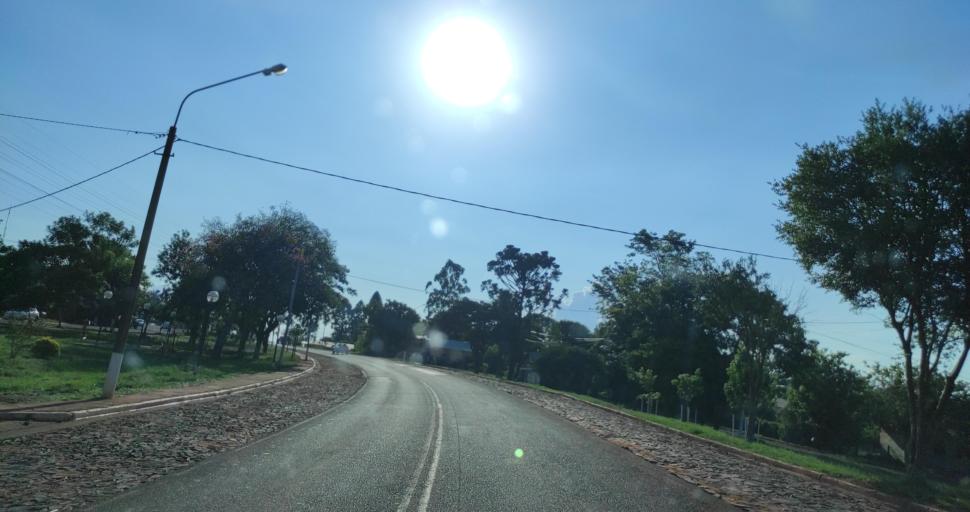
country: AR
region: Misiones
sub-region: Departamento de Eldorado
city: Eldorado
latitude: -26.4145
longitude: -54.4953
